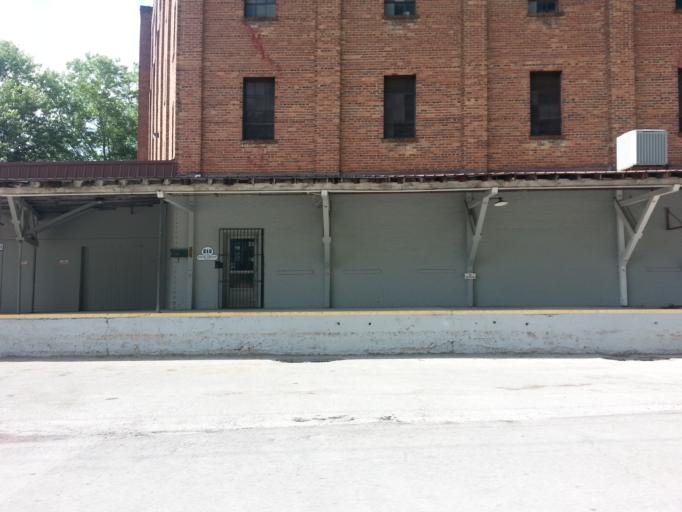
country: US
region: Kentucky
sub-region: Harlan County
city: Harlan
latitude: 36.8435
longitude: -83.3210
